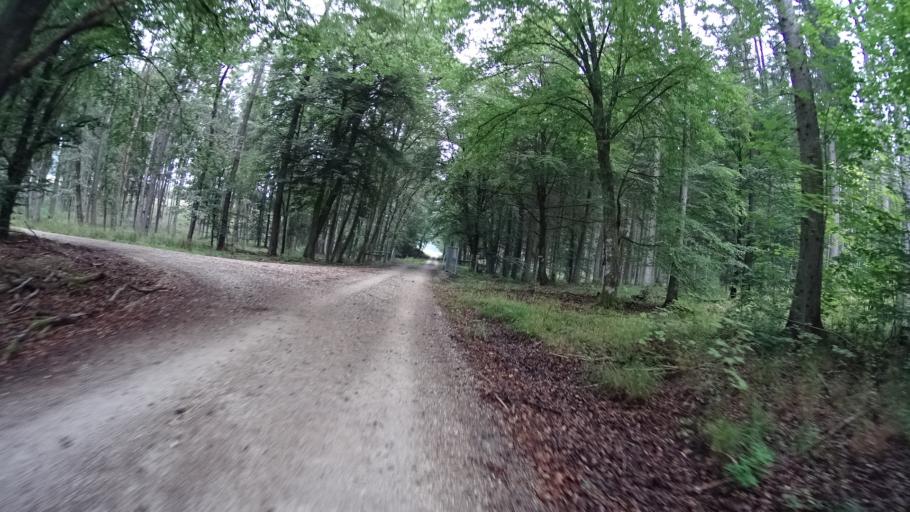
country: DE
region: Bavaria
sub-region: Upper Bavaria
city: Stammham
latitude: 48.8913
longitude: 11.5071
